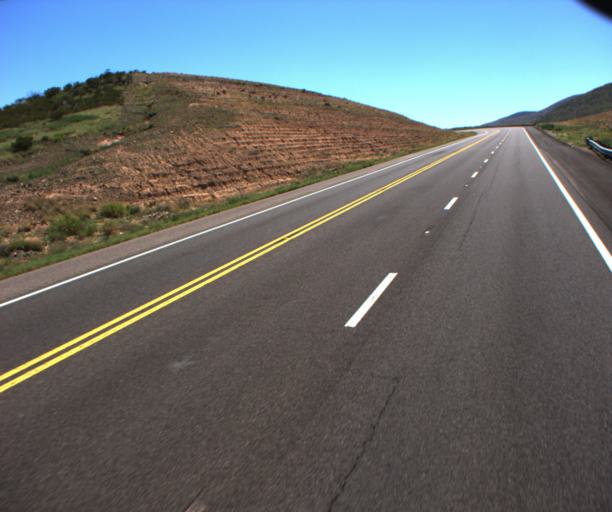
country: US
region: Arizona
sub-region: Greenlee County
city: Clifton
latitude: 32.9169
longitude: -109.2500
